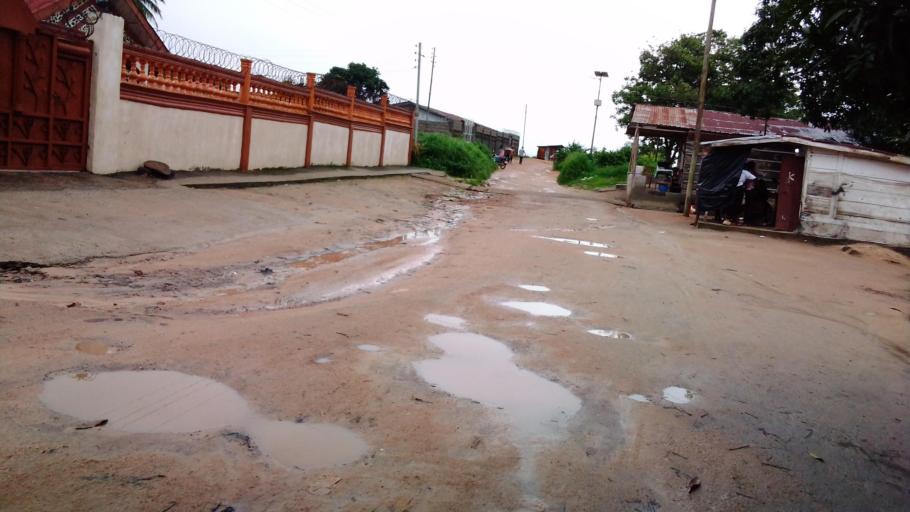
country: SL
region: Eastern Province
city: Kenema
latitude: 7.8985
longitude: -11.1842
